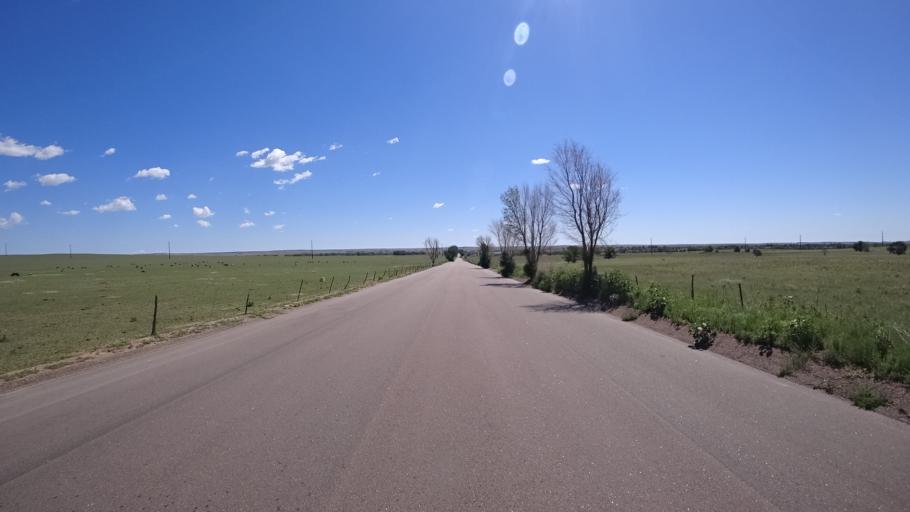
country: US
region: Colorado
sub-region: El Paso County
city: Security-Widefield
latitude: 38.7809
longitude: -104.6723
